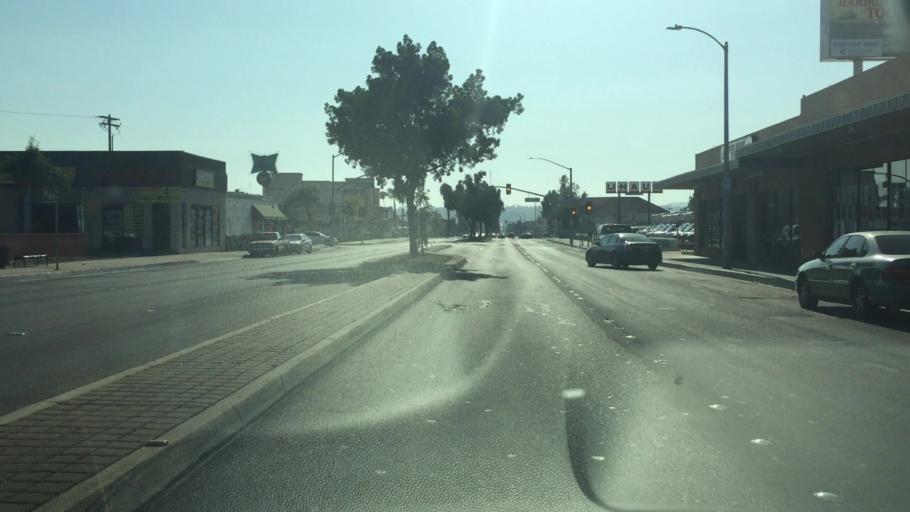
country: US
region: California
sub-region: San Diego County
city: Bostonia
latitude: 32.7950
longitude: -116.9404
